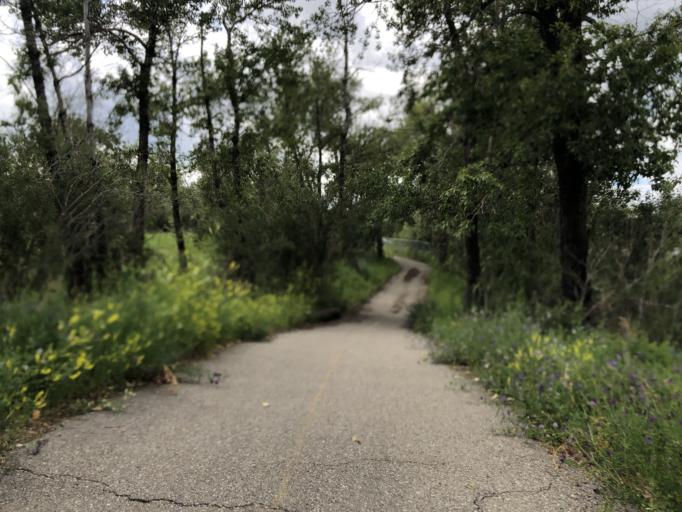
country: CA
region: Alberta
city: Calgary
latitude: 51.0066
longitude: -114.0196
